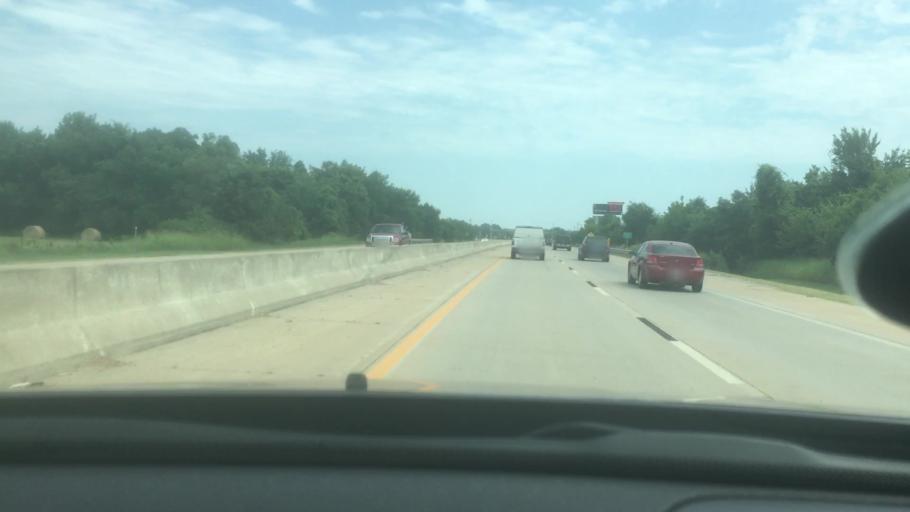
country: US
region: Oklahoma
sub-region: Pottawatomie County
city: Shawnee
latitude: 35.2994
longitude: -96.9435
